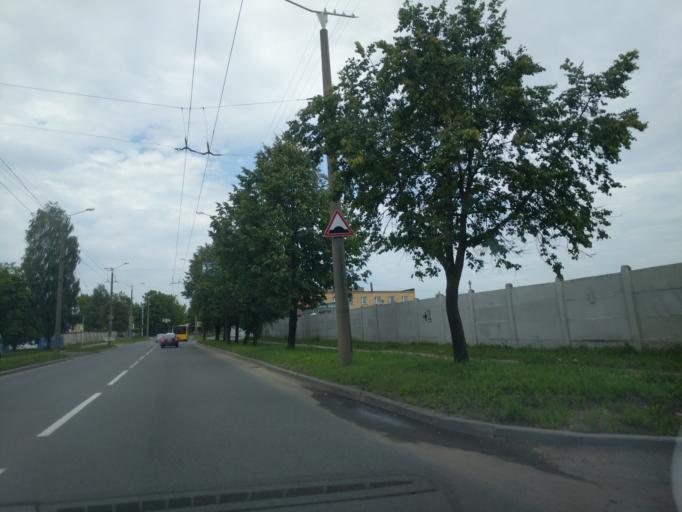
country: BY
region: Minsk
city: Novoye Medvezhino
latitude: 53.8871
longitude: 27.4806
